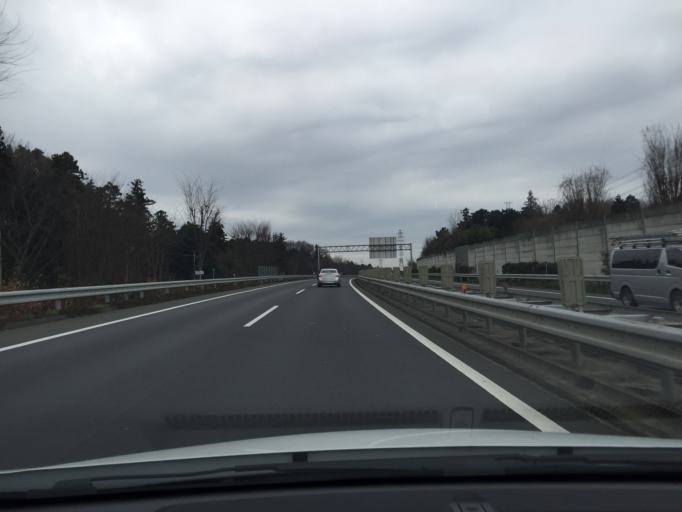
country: JP
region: Saitama
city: Sayama
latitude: 35.9012
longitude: 139.3901
